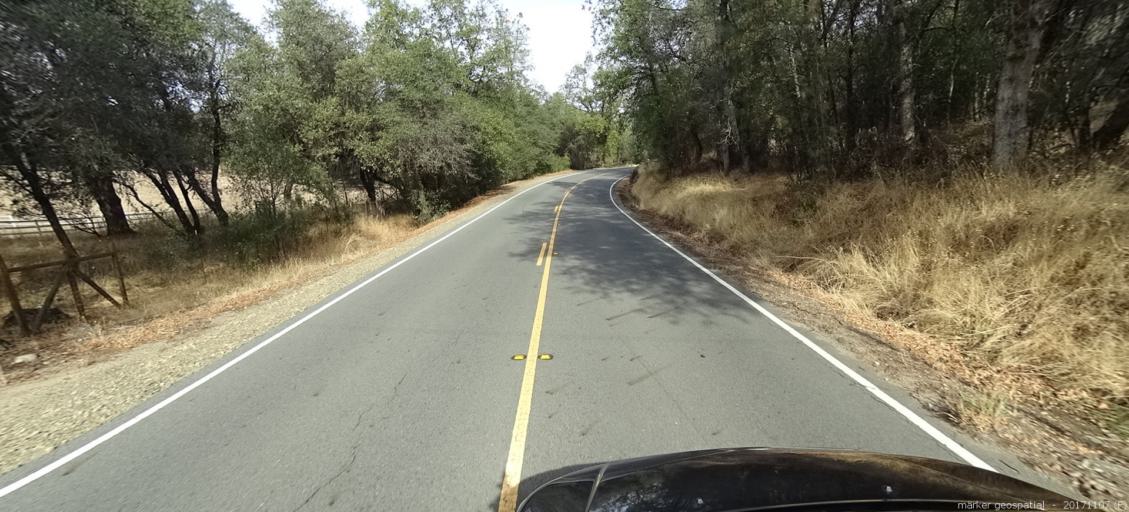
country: US
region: California
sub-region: Shasta County
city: Shasta
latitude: 40.4930
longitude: -122.5484
